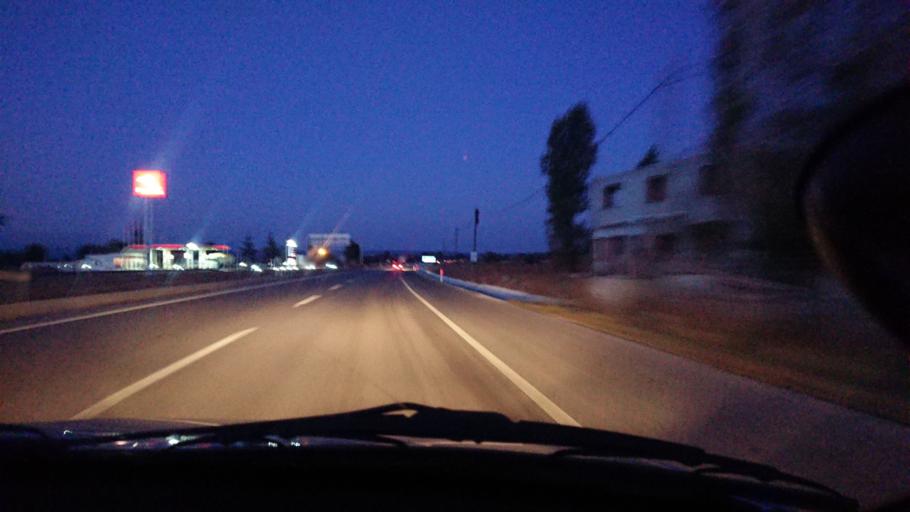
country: TR
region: Kuetahya
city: Cavdarhisar
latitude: 39.2041
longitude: 29.6342
